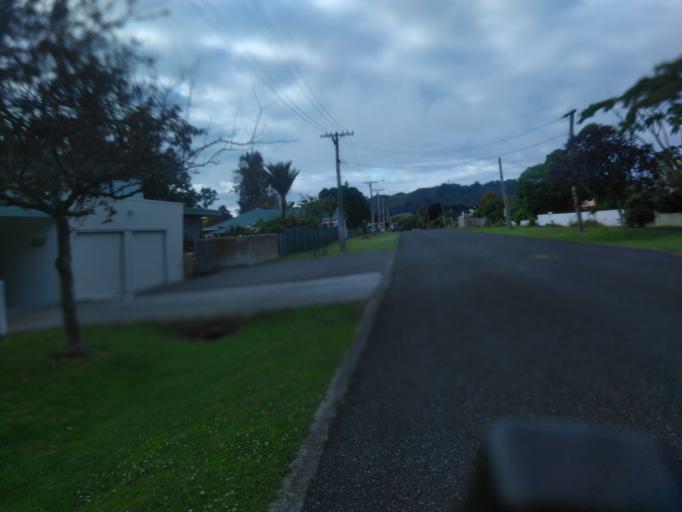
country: NZ
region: Gisborne
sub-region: Gisborne District
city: Gisborne
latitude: -38.6615
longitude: 178.0315
